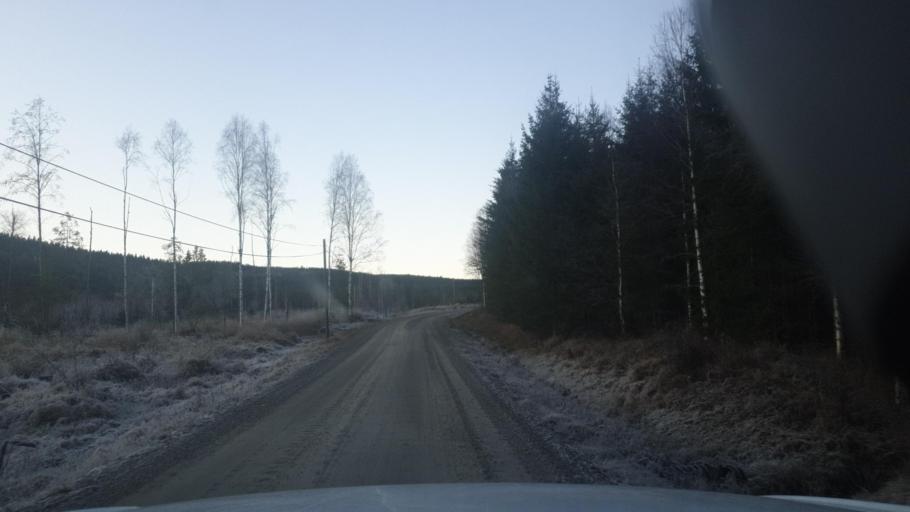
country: SE
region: Vaermland
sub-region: Eda Kommun
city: Charlottenberg
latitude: 59.9715
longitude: 12.4995
